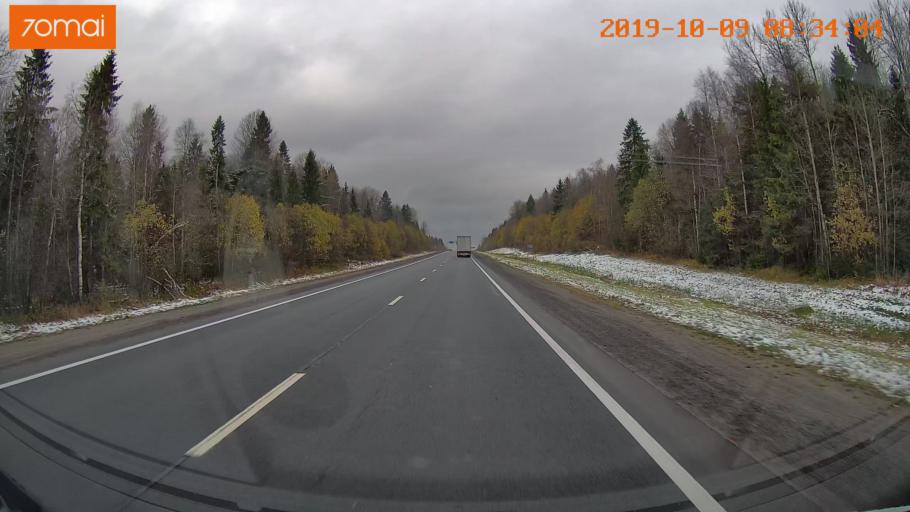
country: RU
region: Vologda
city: Gryazovets
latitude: 58.8915
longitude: 40.1880
